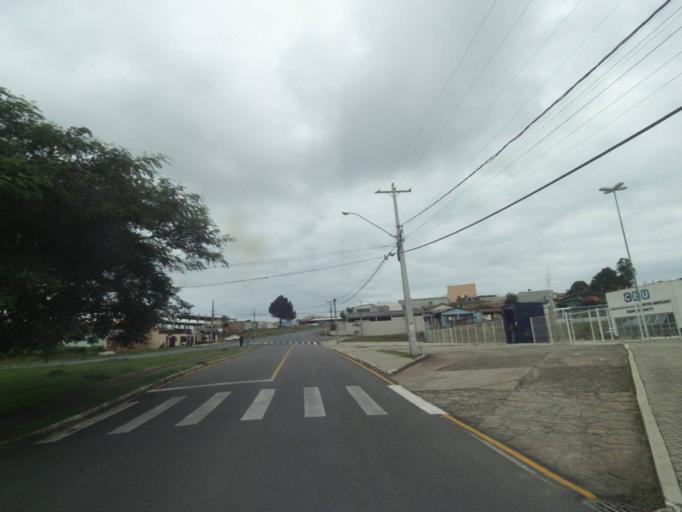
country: BR
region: Parana
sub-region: Quatro Barras
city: Quatro Barras
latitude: -25.3537
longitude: -49.1111
